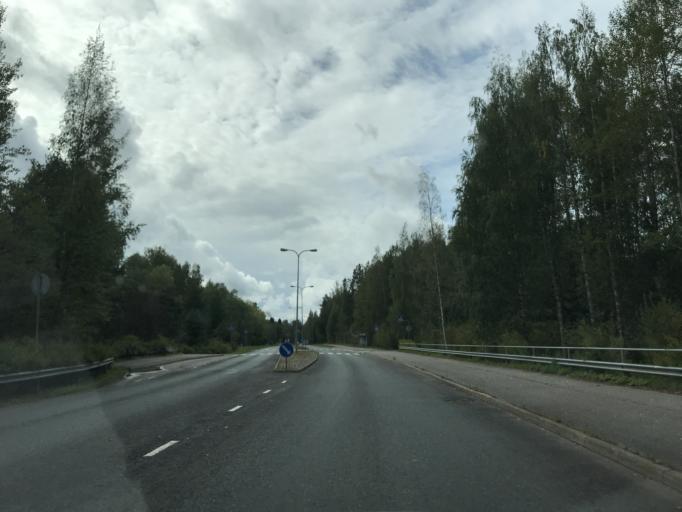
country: FI
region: Paijanne Tavastia
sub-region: Lahti
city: Lahti
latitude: 60.9963
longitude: 25.7500
